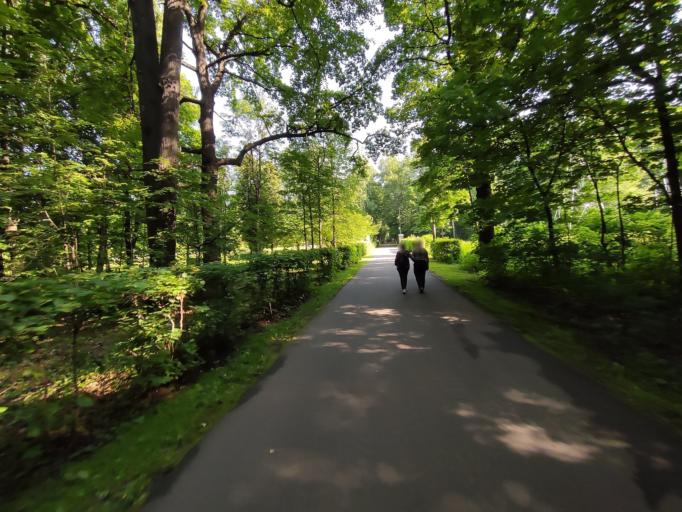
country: RU
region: Moscow
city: Metrogorodok
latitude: 55.7794
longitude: 37.7530
